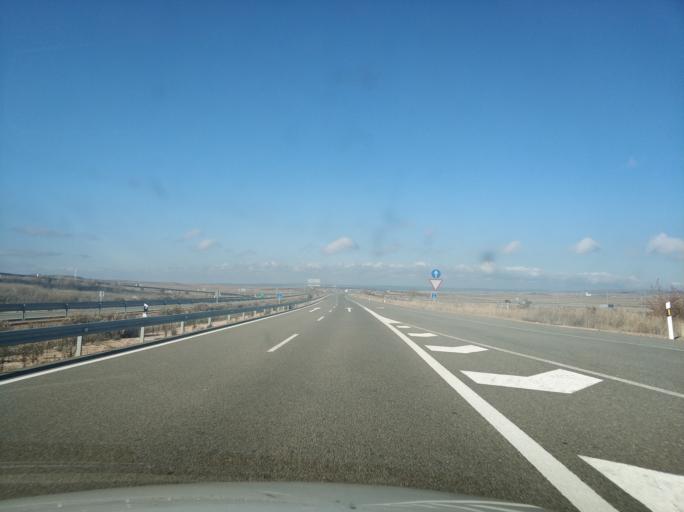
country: ES
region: Castille and Leon
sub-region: Provincia de Soria
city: Adradas
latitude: 41.3852
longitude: -2.4674
